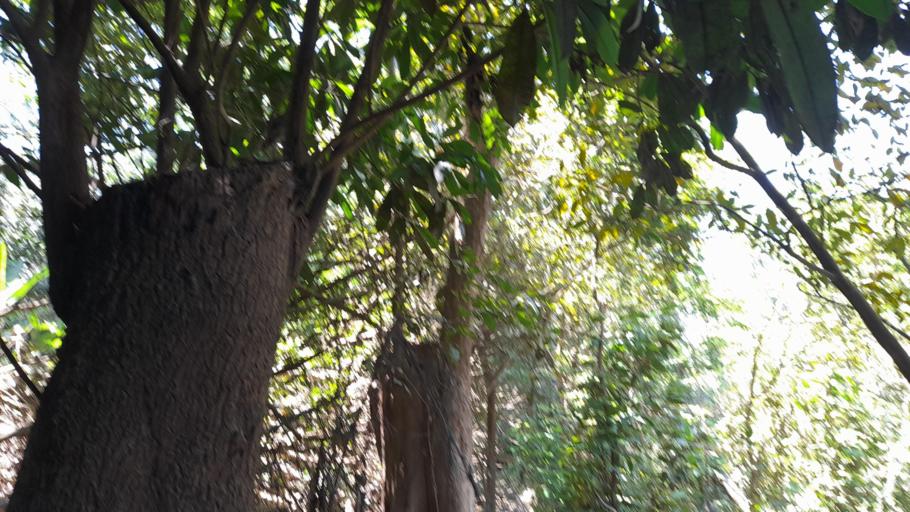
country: PE
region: Ucayali
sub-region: Provincia de Coronel Portillo
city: Puerto Callao
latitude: -8.2597
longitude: -74.6408
